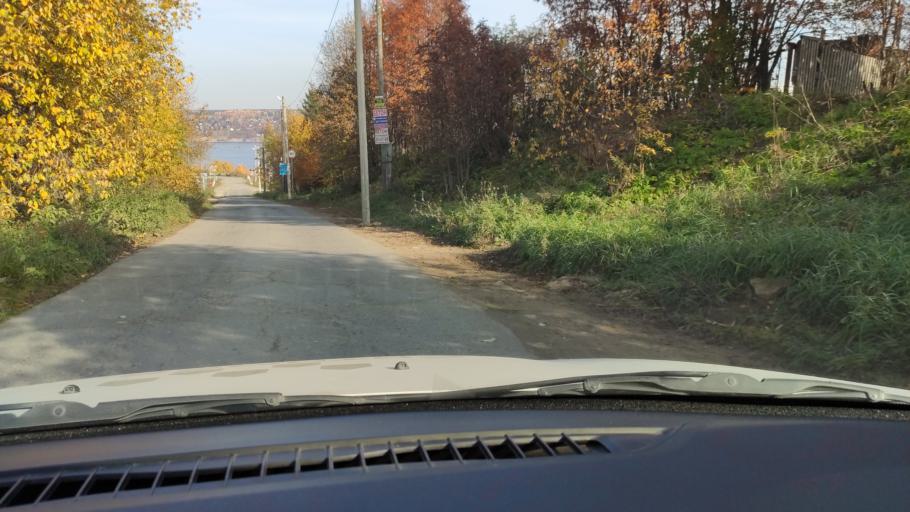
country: RU
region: Perm
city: Sylva
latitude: 58.0405
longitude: 56.7490
